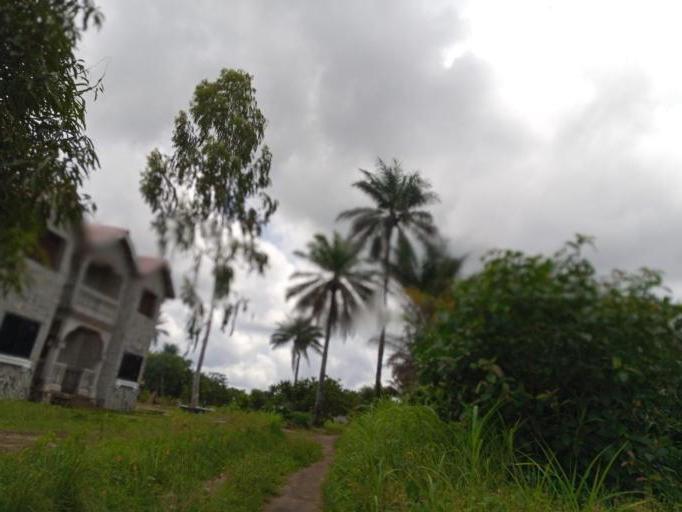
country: SL
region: Northern Province
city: Masoyila
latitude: 8.5884
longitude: -13.1706
